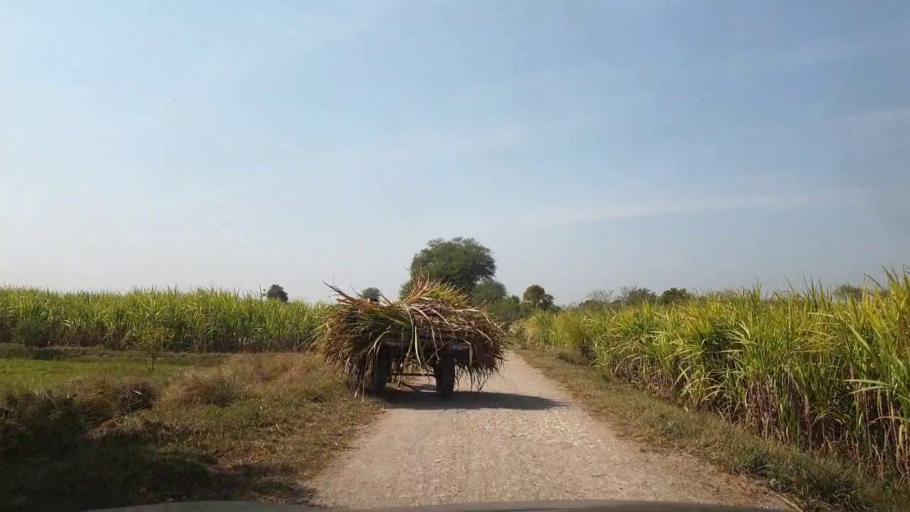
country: PK
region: Sindh
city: Tando Adam
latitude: 25.6368
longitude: 68.7190
